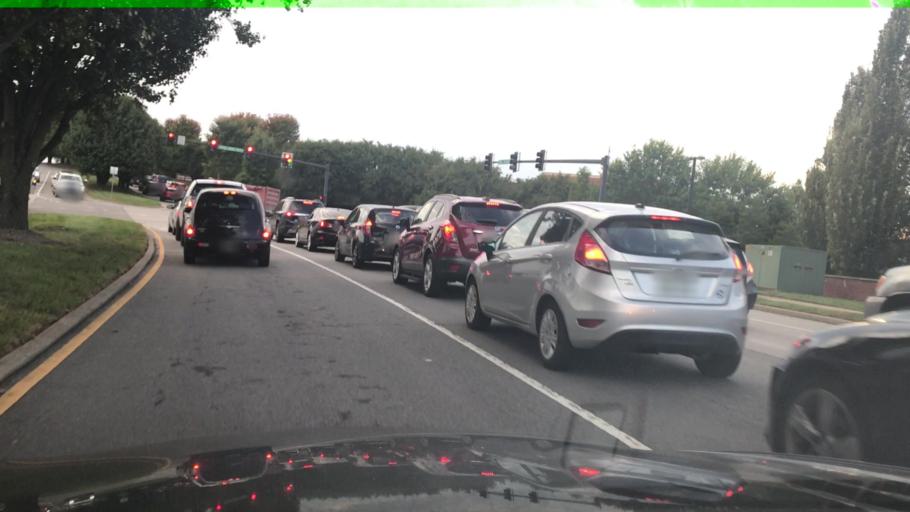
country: US
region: Tennessee
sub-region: Williamson County
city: Franklin
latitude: 35.9452
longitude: -86.8281
